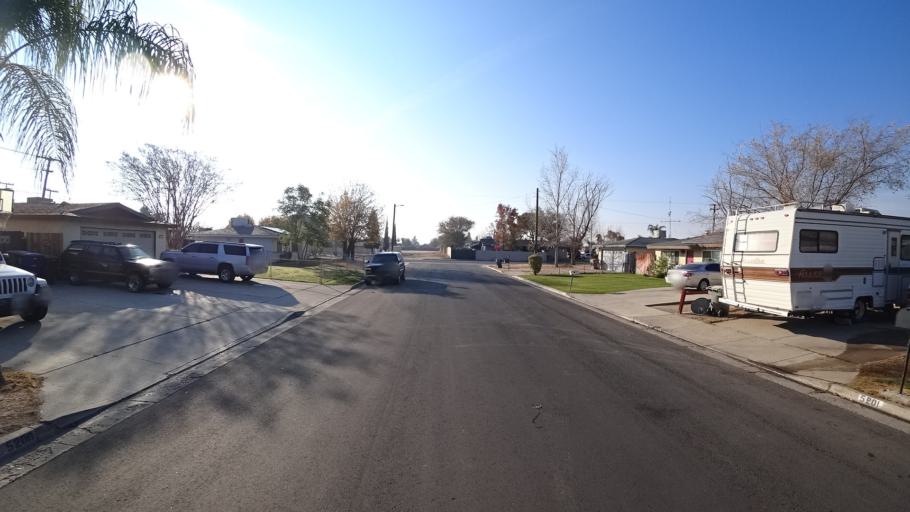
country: US
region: California
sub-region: Kern County
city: Greenfield
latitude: 35.3073
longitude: -119.0223
